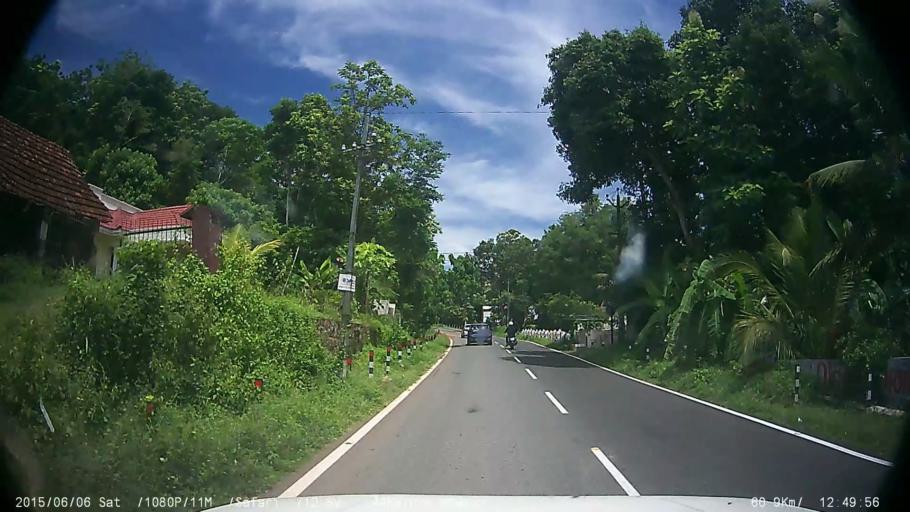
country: IN
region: Kerala
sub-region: Kottayam
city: Kottayam
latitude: 9.5362
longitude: 76.5670
